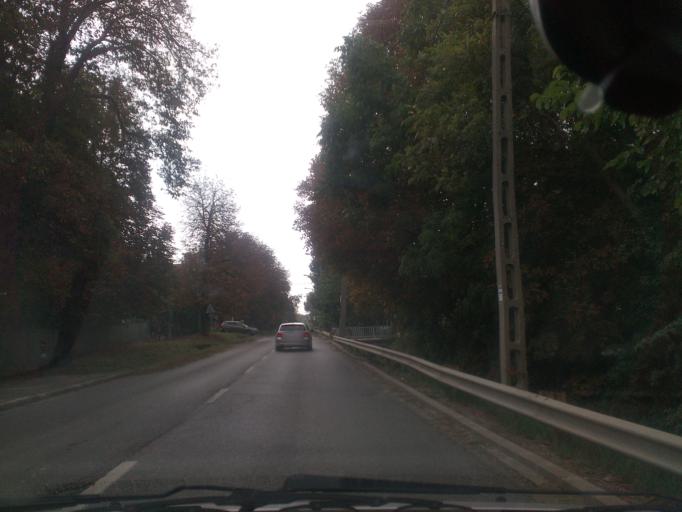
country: HU
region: Pest
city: Solymar
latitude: 47.5625
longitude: 18.9632
